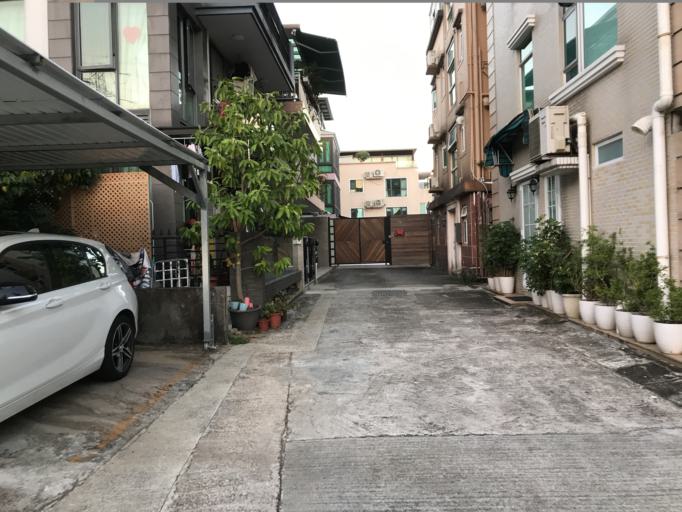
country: HK
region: Tai Po
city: Tai Po
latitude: 22.4693
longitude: 114.1474
